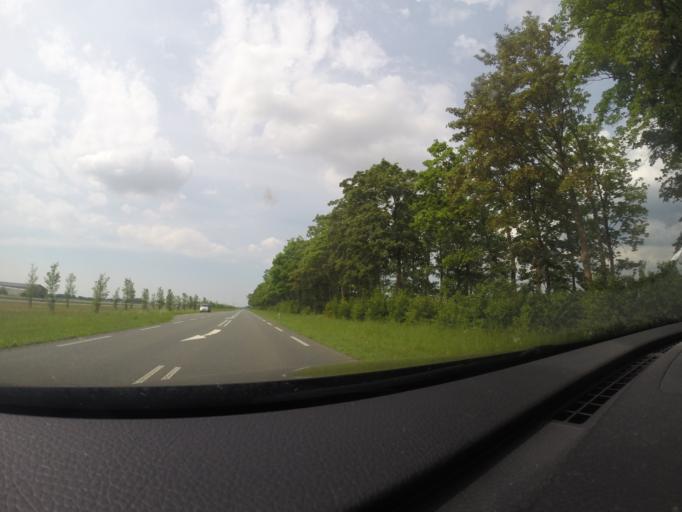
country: NL
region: Flevoland
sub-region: Gemeente Noordoostpolder
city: Ens
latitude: 52.6285
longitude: 5.8298
